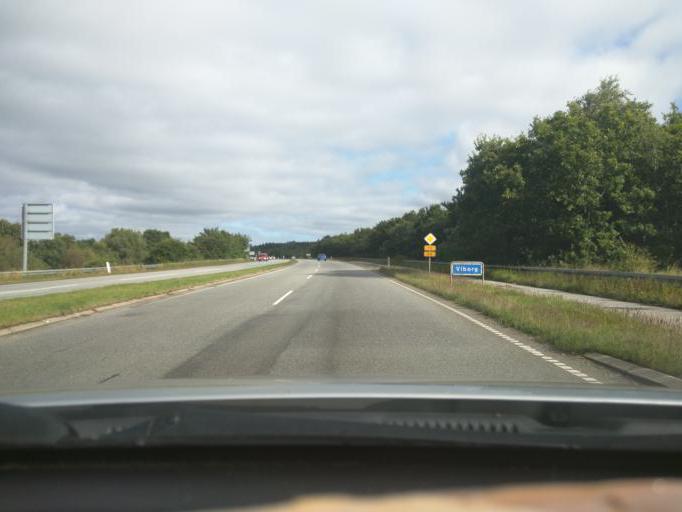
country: DK
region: Central Jutland
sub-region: Viborg Kommune
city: Viborg
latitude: 56.4272
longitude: 9.3901
